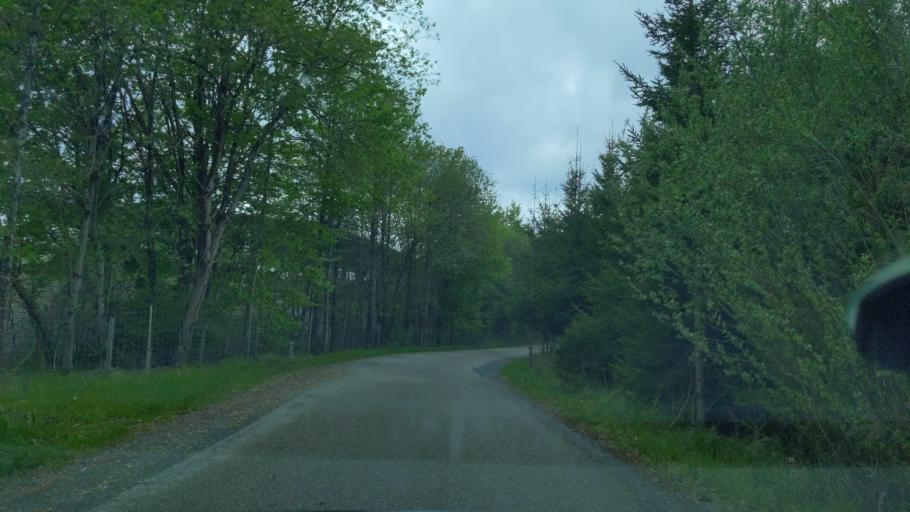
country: DE
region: Bavaria
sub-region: Upper Bavaria
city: Ebersberg
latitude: 48.1111
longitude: 11.9862
